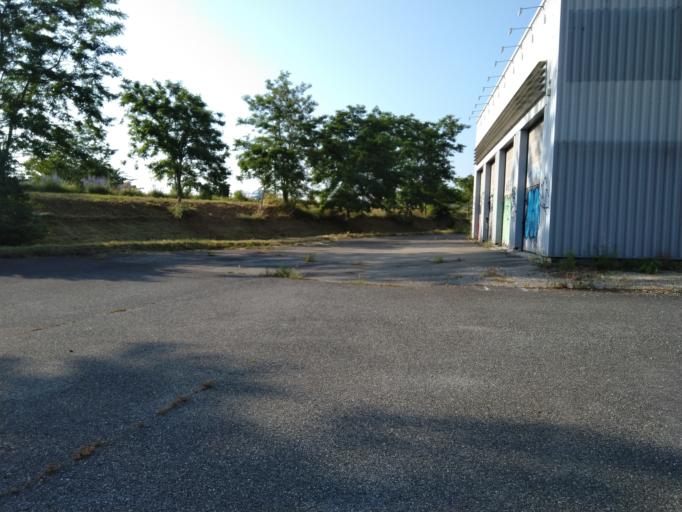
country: FR
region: Midi-Pyrenees
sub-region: Departement de la Haute-Garonne
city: Ramonville-Saint-Agne
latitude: 43.5399
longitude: 1.4813
